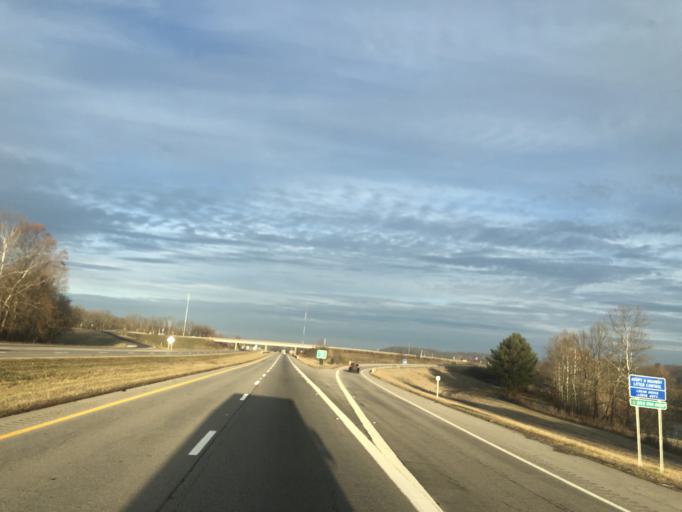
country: US
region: Ohio
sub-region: Hocking County
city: Logan
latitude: 39.5198
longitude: -82.3729
